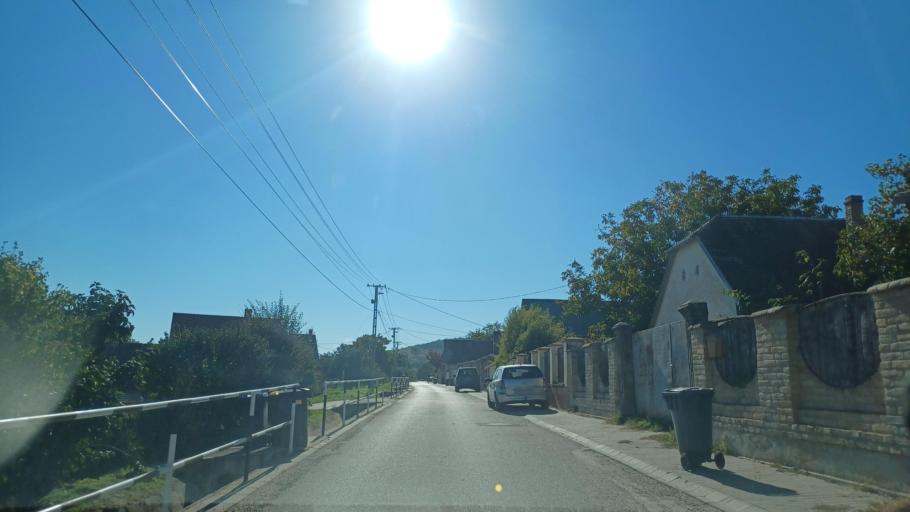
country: HU
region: Tolna
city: Szekszard
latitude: 46.3131
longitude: 18.6921
